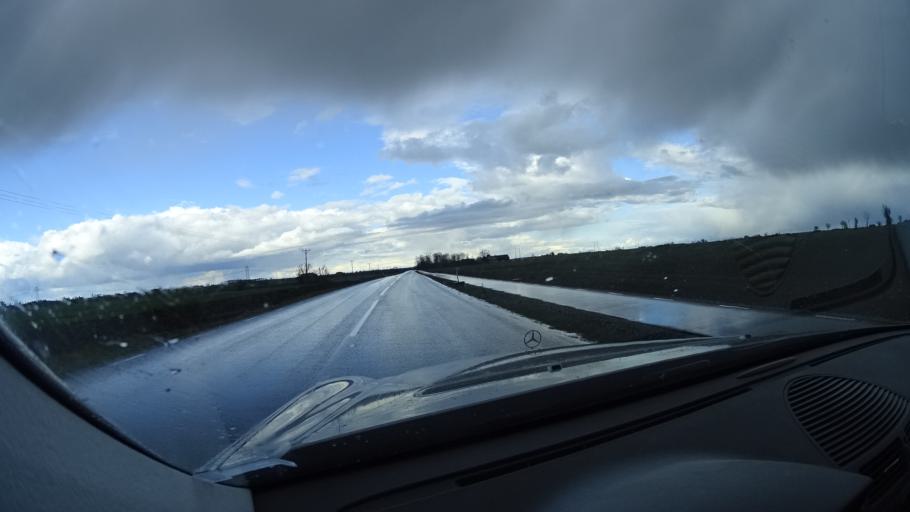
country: SE
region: Skane
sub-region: Eslovs Kommun
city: Eslov
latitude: 55.7943
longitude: 13.2559
